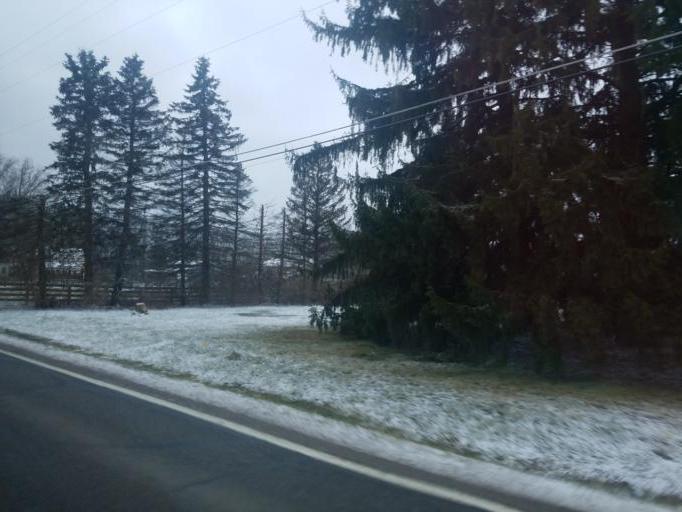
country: US
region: Ohio
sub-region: Franklin County
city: New Albany
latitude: 40.0255
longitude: -82.7893
